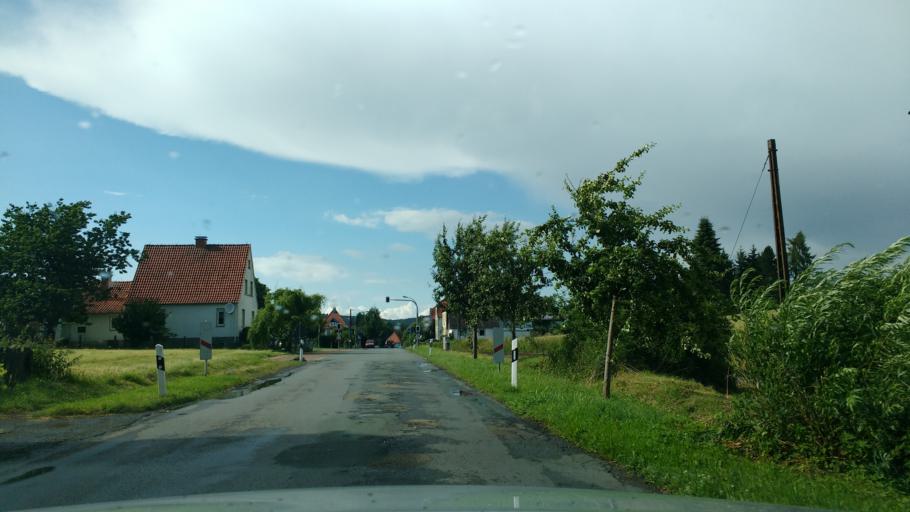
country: DE
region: North Rhine-Westphalia
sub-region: Regierungsbezirk Detmold
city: Barntrup
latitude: 52.0268
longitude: 9.1267
